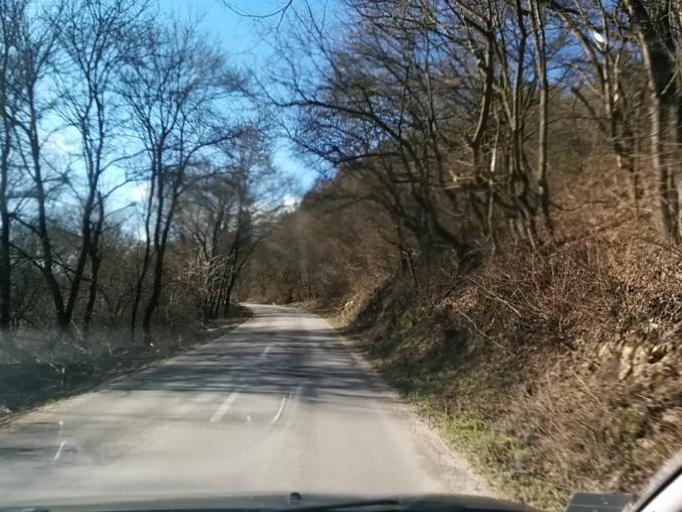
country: SK
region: Nitriansky
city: Cachtice
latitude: 48.7224
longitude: 17.7391
